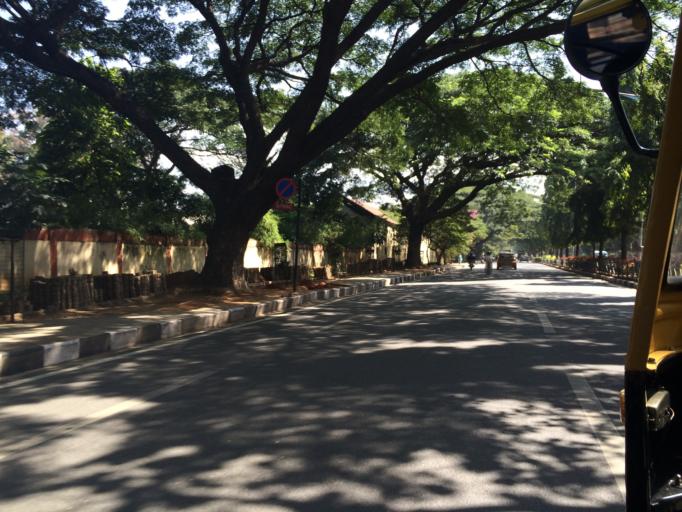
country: IN
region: Karnataka
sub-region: Bangalore Urban
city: Bangalore
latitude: 12.9769
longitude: 77.6097
